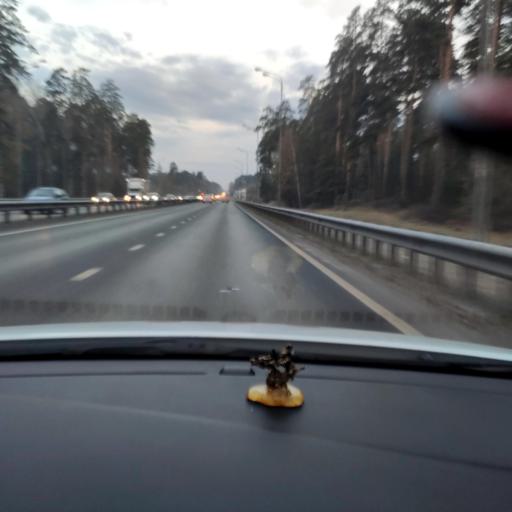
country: RU
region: Tatarstan
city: Staroye Arakchino
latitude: 55.8371
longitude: 48.9717
